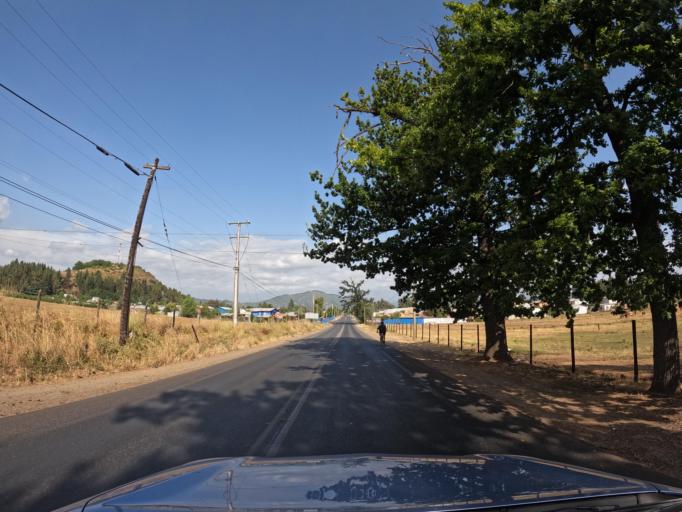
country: CL
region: Maule
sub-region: Provincia de Curico
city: Molina
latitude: -35.2800
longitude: -71.2682
